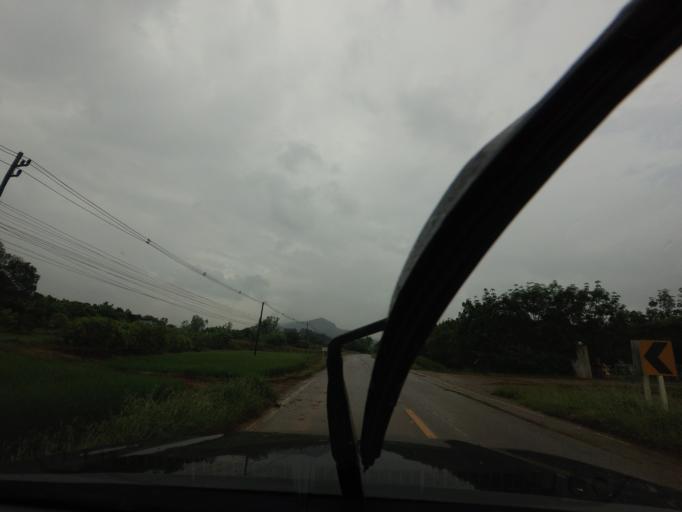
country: TH
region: Loei
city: Pak Chom
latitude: 18.2029
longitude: 102.0648
